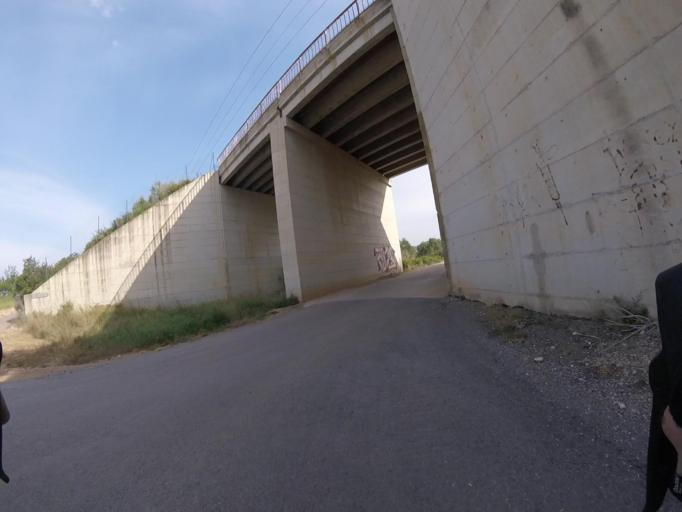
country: ES
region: Valencia
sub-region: Provincia de Castello
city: Alcoceber
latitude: 40.2685
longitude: 0.2521
